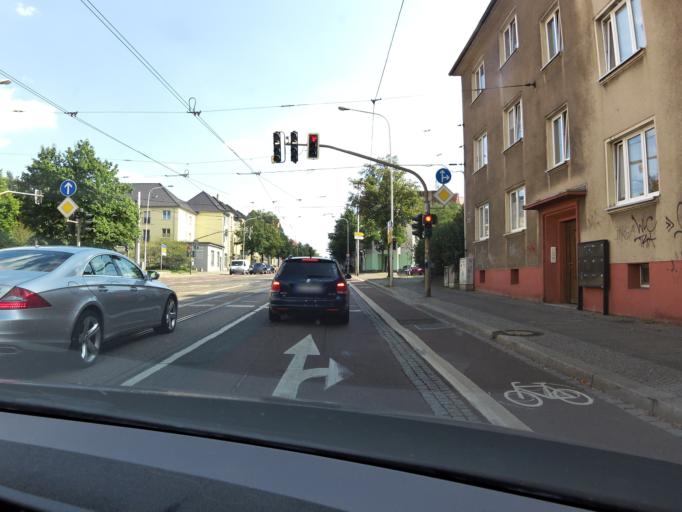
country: DE
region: Saxony-Anhalt
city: Sennewitz
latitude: 51.5105
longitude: 11.9615
